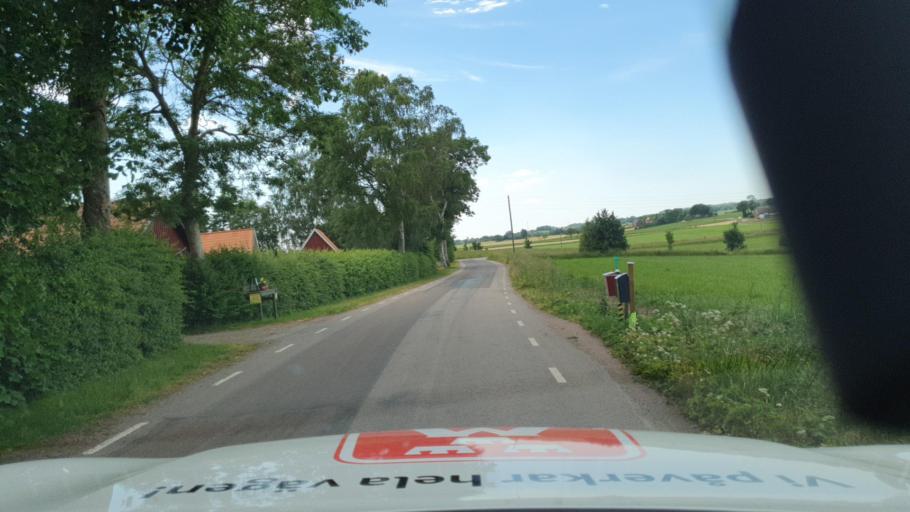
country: SE
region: Skane
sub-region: Sjobo Kommun
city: Sjoebo
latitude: 55.6342
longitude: 13.8119
